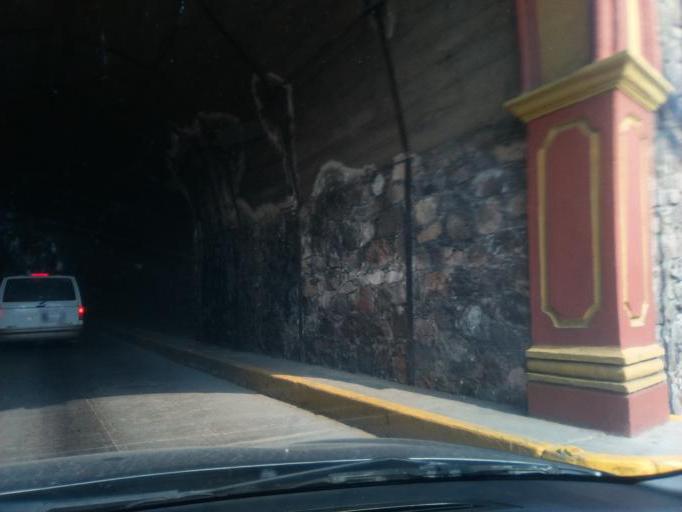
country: MX
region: Guanajuato
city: Guanajuato
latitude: 21.0208
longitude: -101.2604
